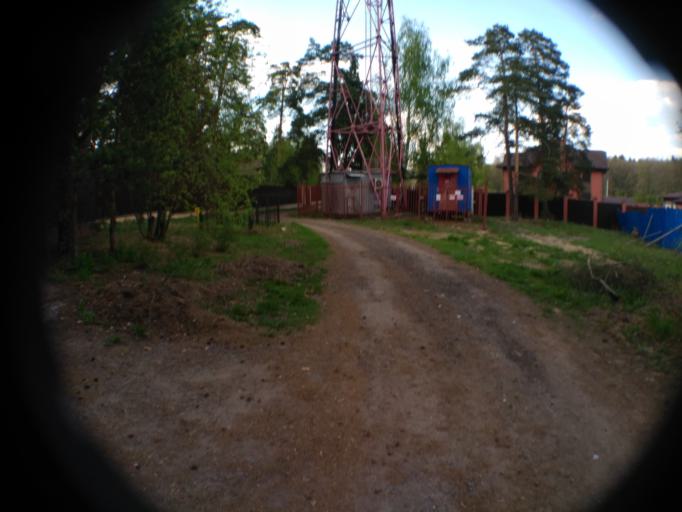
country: RU
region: Moskovskaya
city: Kratovo
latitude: 55.5769
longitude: 38.1701
